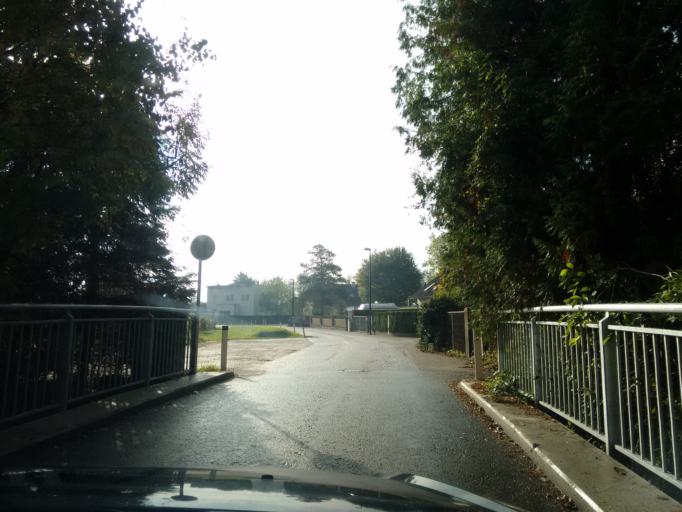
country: AT
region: Upper Austria
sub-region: Wels-Land
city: Gunskirchen
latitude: 48.1638
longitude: 13.9856
